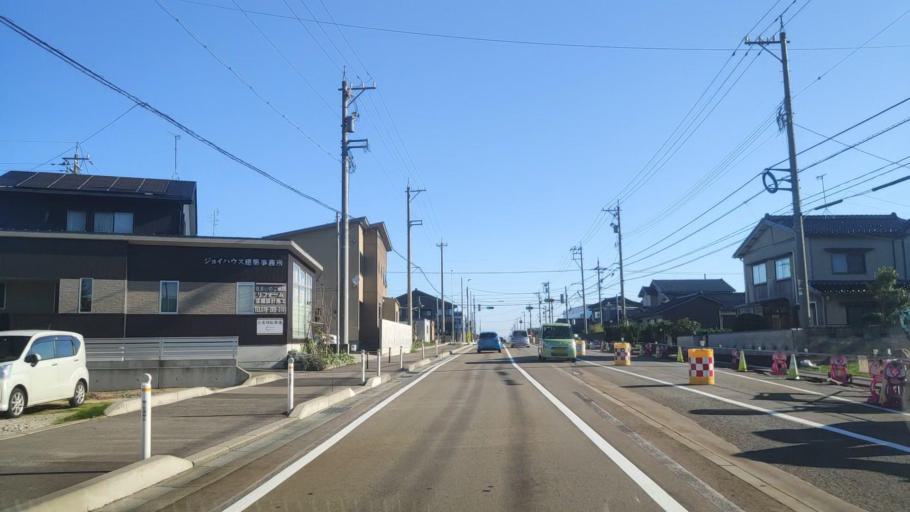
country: JP
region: Ishikawa
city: Tsubata
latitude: 36.7373
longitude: 136.7035
